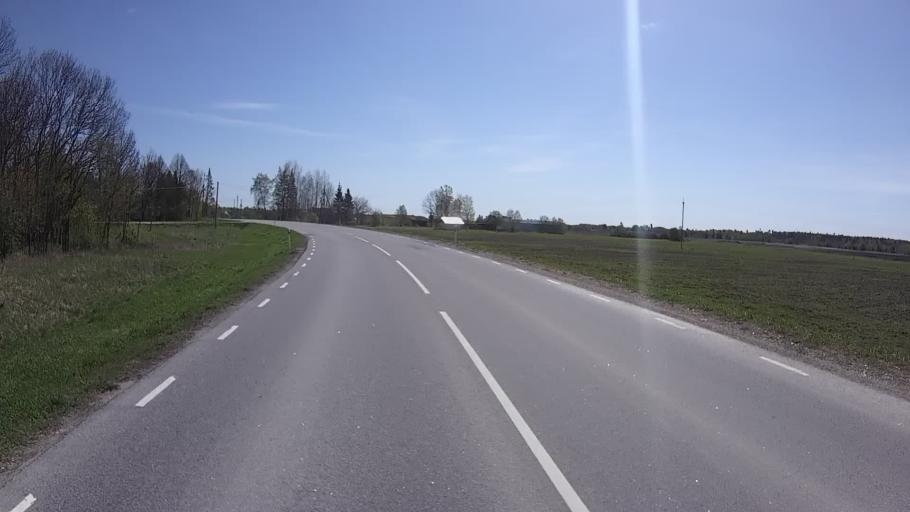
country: EE
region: Harju
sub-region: Keila linn
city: Keila
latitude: 59.3117
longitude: 24.3171
